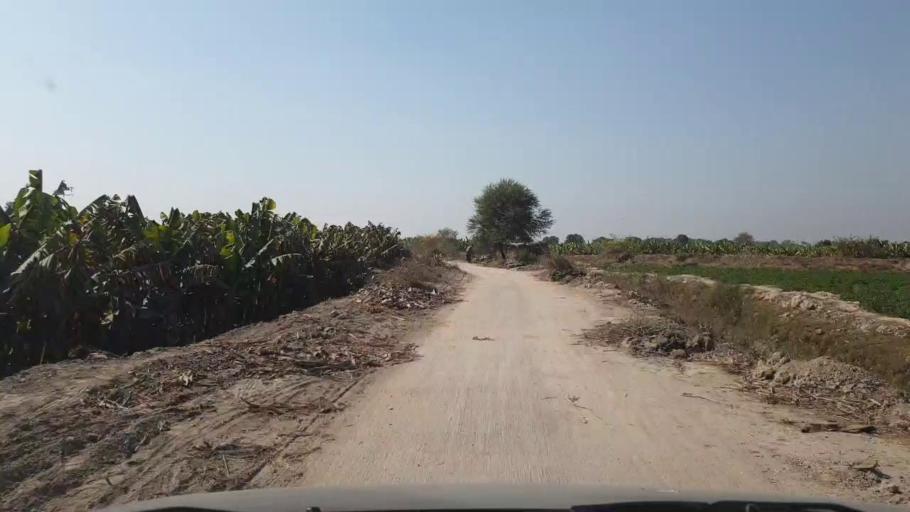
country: PK
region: Sindh
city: Tando Allahyar
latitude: 25.4275
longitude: 68.6348
